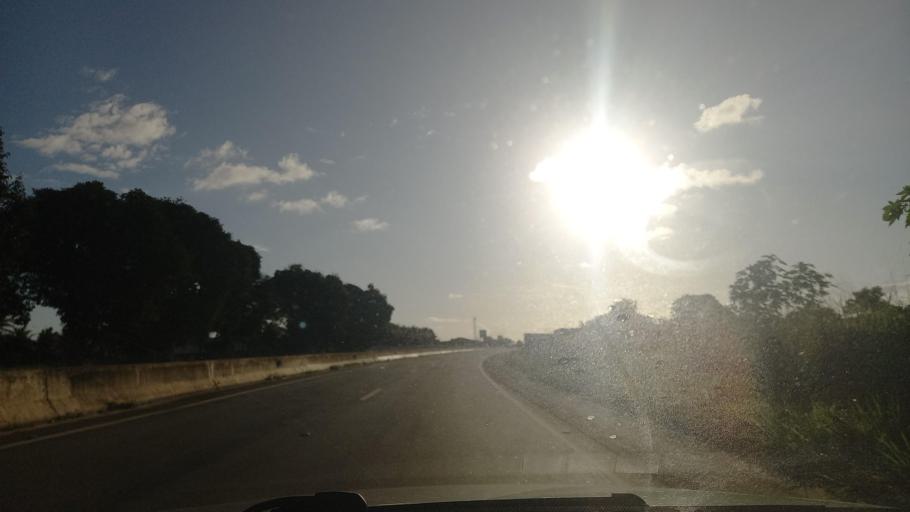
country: BR
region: Alagoas
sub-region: Campo Alegre
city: Campo Alegre
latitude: -9.8036
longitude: -36.2701
